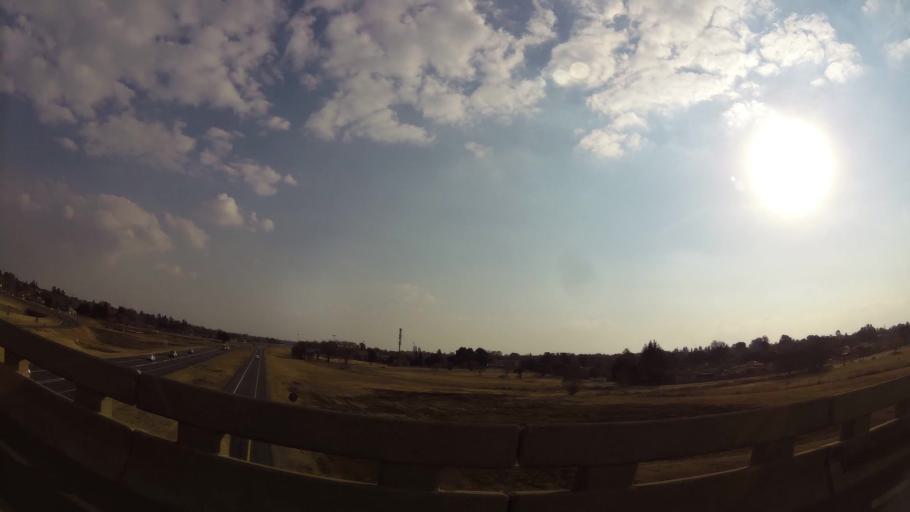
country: ZA
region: Gauteng
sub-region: Ekurhuleni Metropolitan Municipality
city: Springs
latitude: -26.2793
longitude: 28.4528
